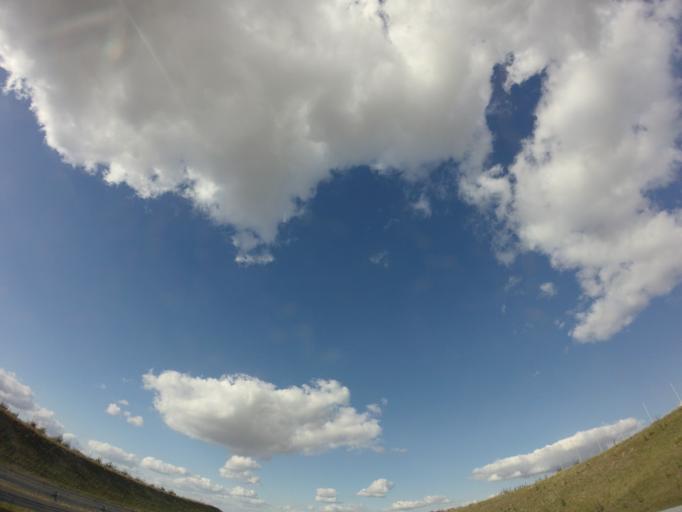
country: PL
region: Lower Silesian Voivodeship
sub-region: Powiat trzebnicki
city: Trzebnica
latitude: 51.3168
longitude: 17.0370
